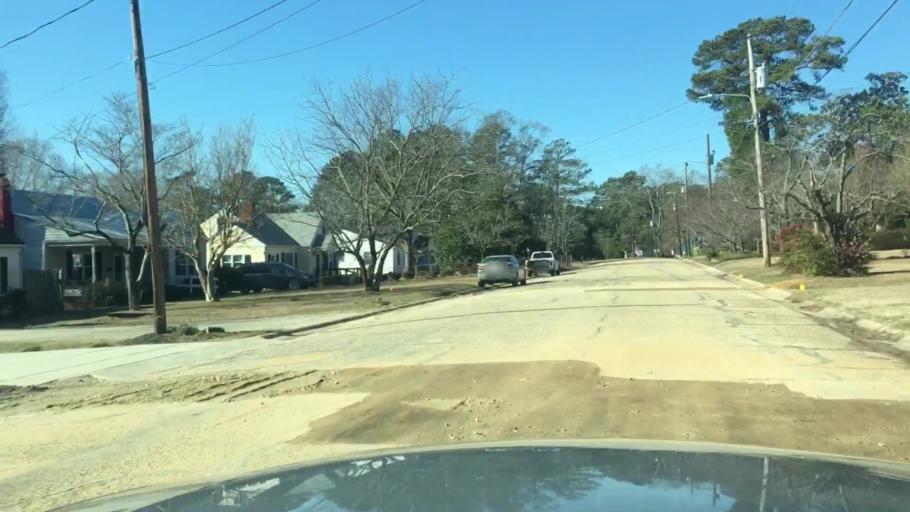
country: US
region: North Carolina
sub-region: Cumberland County
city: Fayetteville
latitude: 35.0718
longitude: -78.9132
